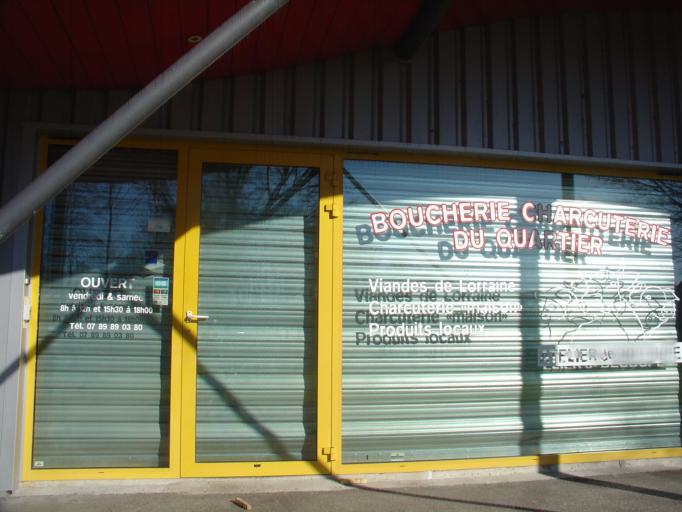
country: FR
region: Lorraine
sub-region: Departement de Meurthe-et-Moselle
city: Blenod-les-Toul
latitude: 48.5466
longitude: 5.7958
